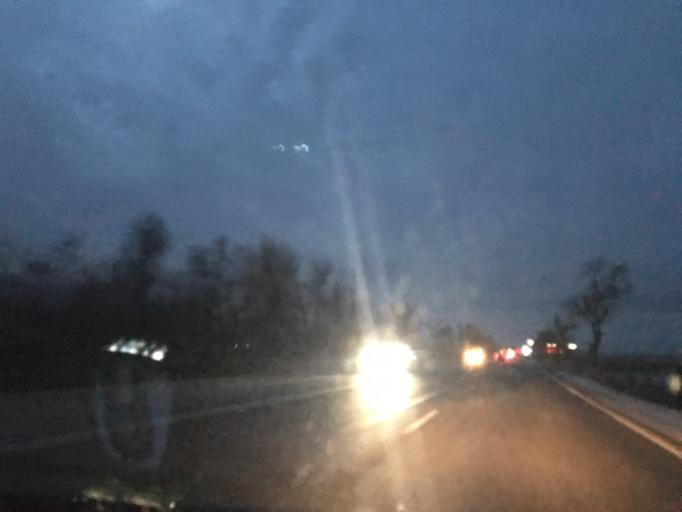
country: RU
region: Rostov
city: Bataysk
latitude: 47.0486
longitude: 39.7434
